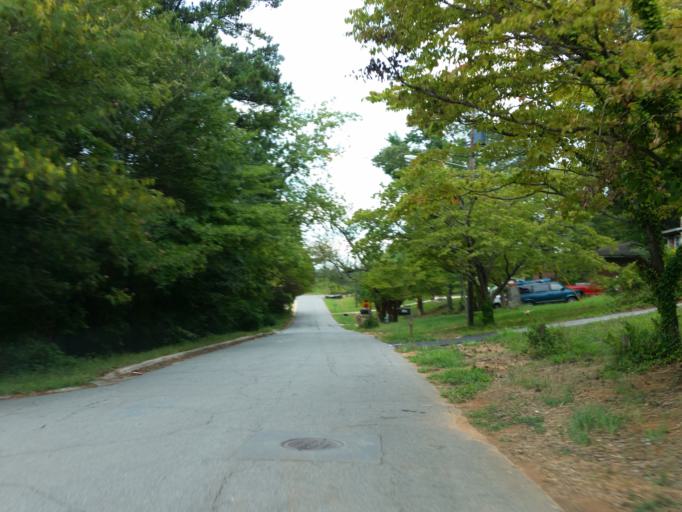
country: US
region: Georgia
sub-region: Cherokee County
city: Woodstock
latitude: 34.0314
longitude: -84.5310
